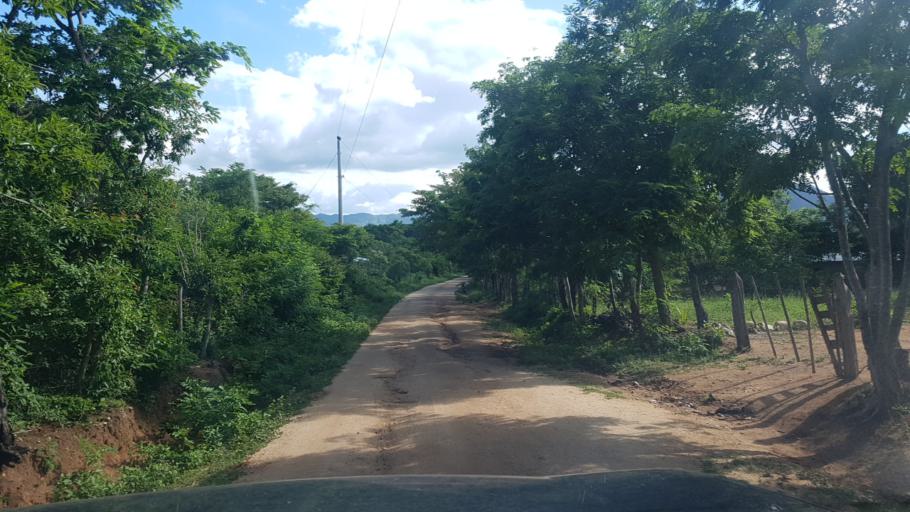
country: NI
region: Nueva Segovia
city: Mozonte
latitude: 13.6548
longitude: -86.3982
